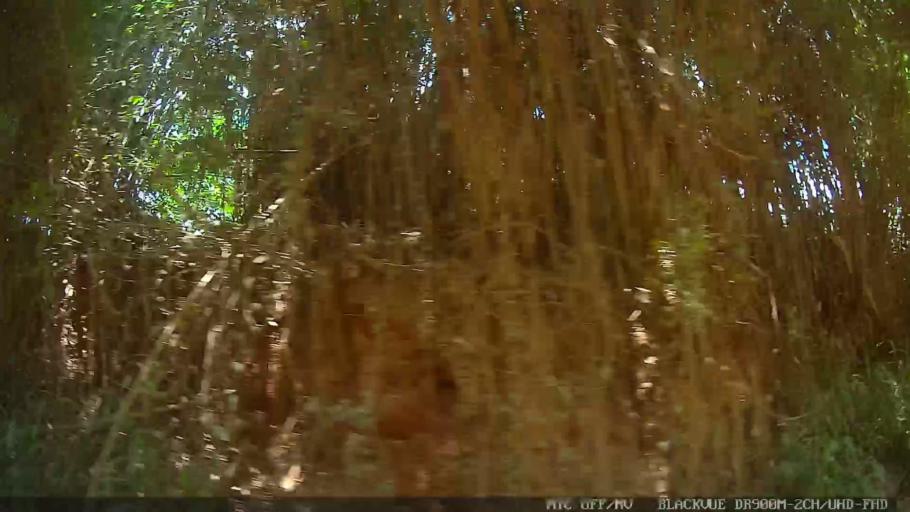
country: BR
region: Sao Paulo
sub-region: Atibaia
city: Atibaia
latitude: -23.1206
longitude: -46.6226
